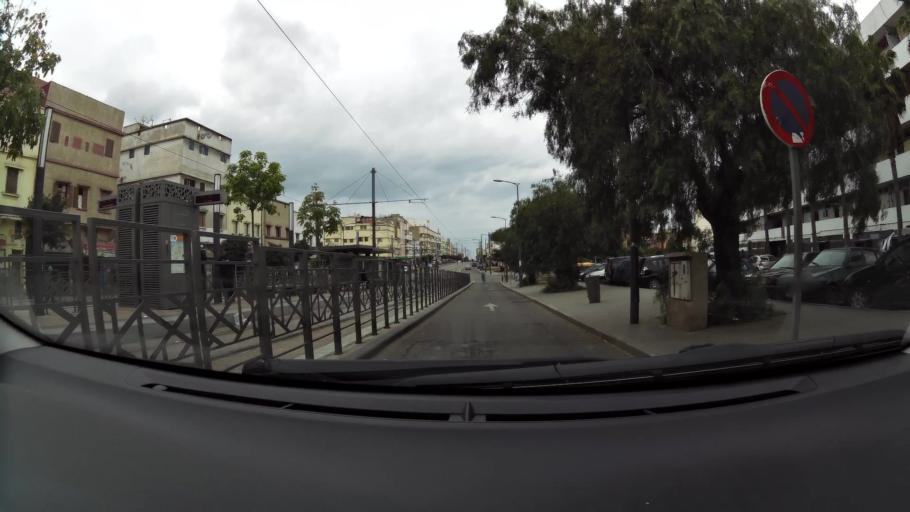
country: MA
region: Grand Casablanca
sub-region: Casablanca
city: Casablanca
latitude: 33.5853
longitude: -7.5665
